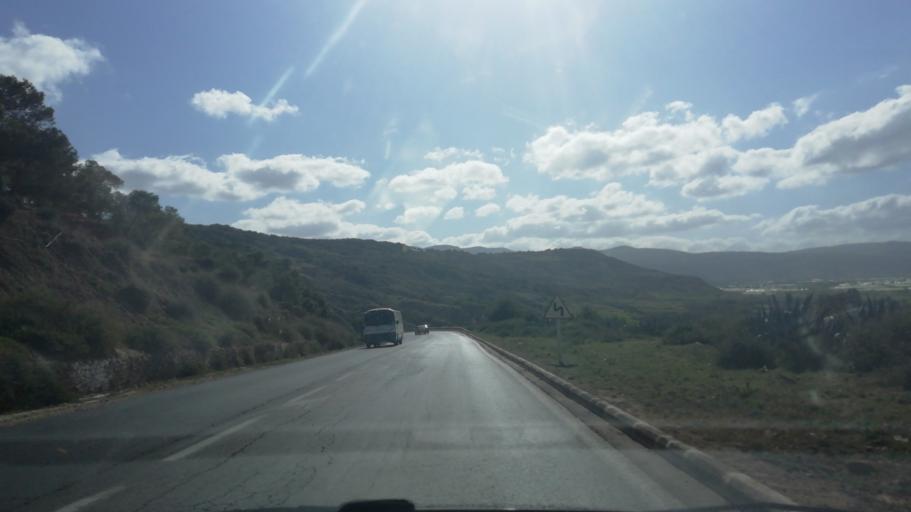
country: DZ
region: Relizane
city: Mazouna
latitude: 36.3082
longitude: 0.6687
